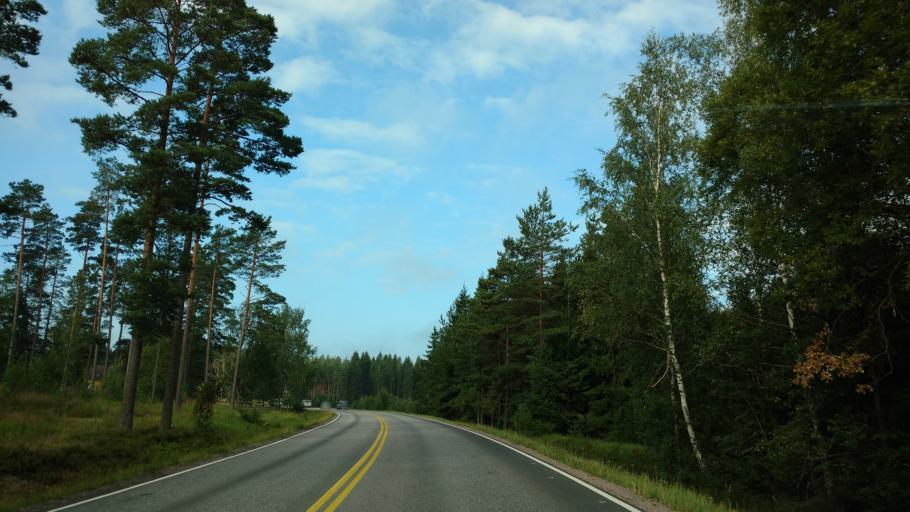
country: FI
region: Varsinais-Suomi
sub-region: Aboland-Turunmaa
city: Vaestanfjaerd
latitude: 60.1279
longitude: 22.6323
